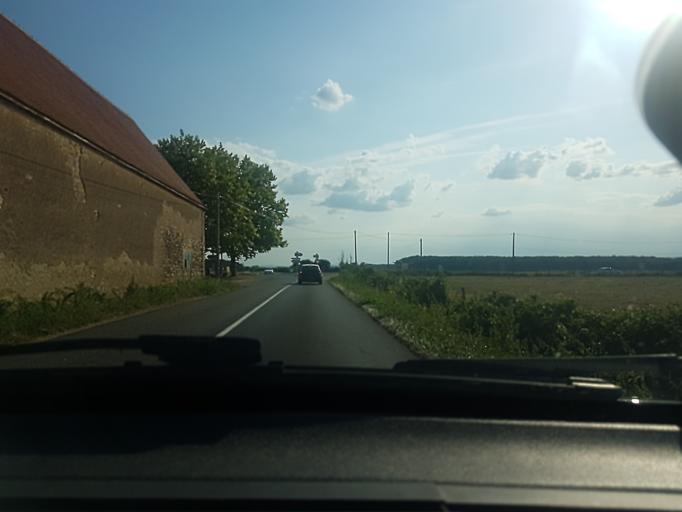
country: FR
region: Bourgogne
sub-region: Departement de Saone-et-Loire
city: Sennecey-le-Grand
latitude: 46.6724
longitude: 4.8148
